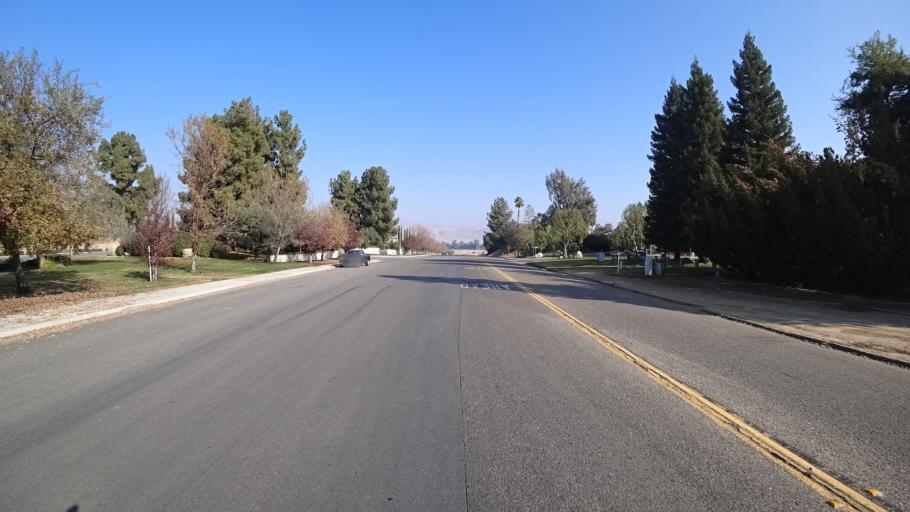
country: US
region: California
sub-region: Kern County
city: Oildale
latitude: 35.4309
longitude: -118.8688
